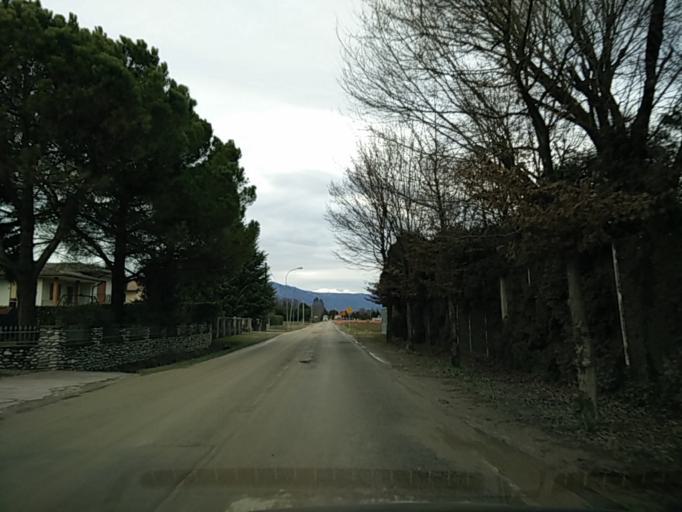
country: IT
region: Veneto
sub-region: Provincia di Treviso
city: Loria Bessica
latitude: 45.7527
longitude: 11.8793
